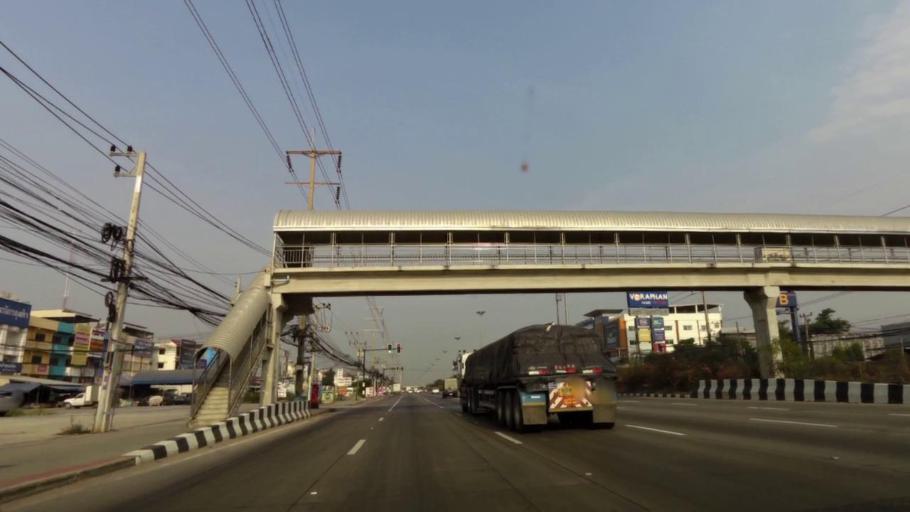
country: TH
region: Phra Nakhon Si Ayutthaya
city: Uthai
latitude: 14.3231
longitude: 100.6303
